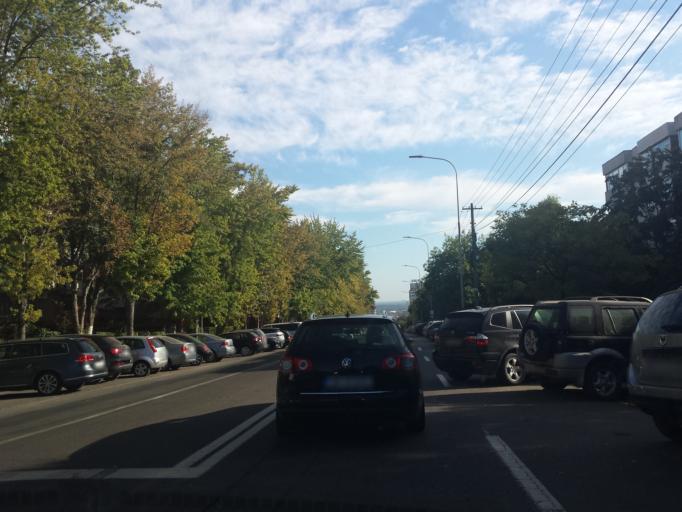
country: RO
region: Tulcea
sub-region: Municipiul Tulcea
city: Tulcea
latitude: 45.1596
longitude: 28.7843
